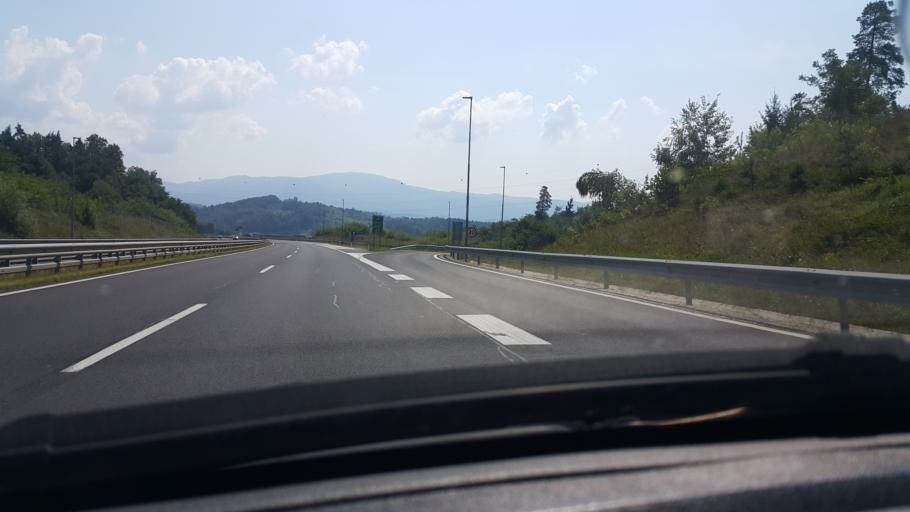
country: SI
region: Novo Mesto
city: Novo Mesto
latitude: 45.8306
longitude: 15.1775
